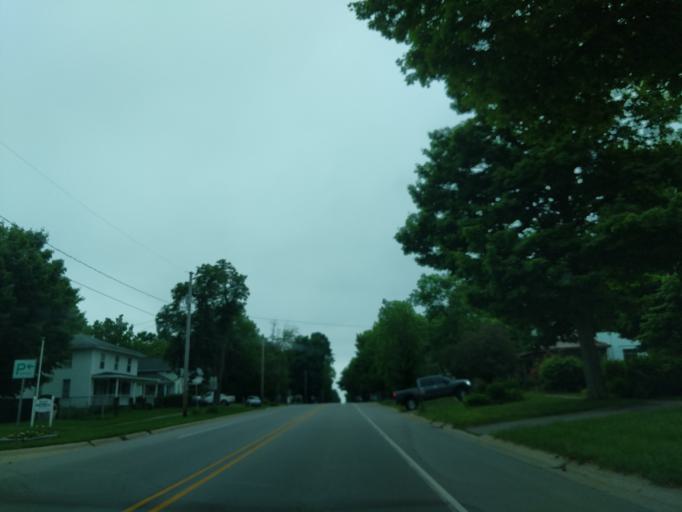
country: US
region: Michigan
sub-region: Hillsdale County
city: Litchfield
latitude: 41.9568
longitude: -84.7703
